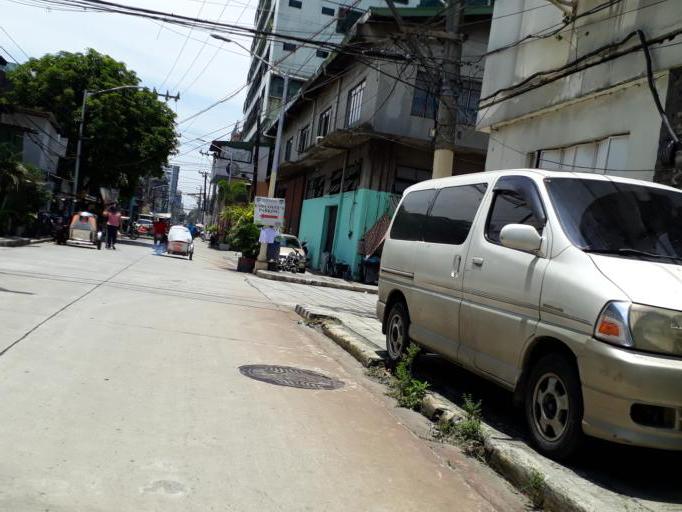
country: PH
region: Calabarzon
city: Del Monte
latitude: 14.6500
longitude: 120.9900
